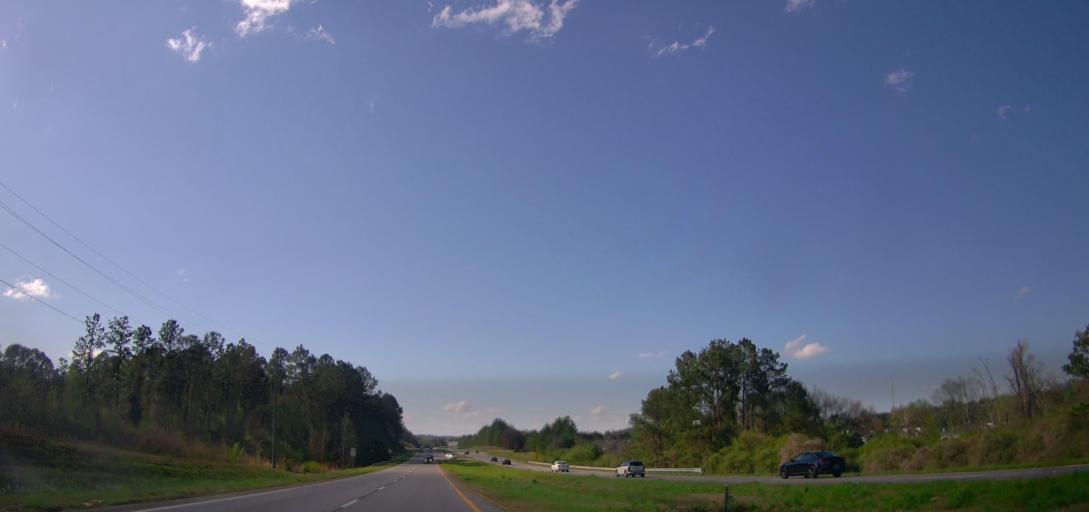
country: US
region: Georgia
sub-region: Baldwin County
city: Milledgeville
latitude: 33.0737
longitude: -83.2521
